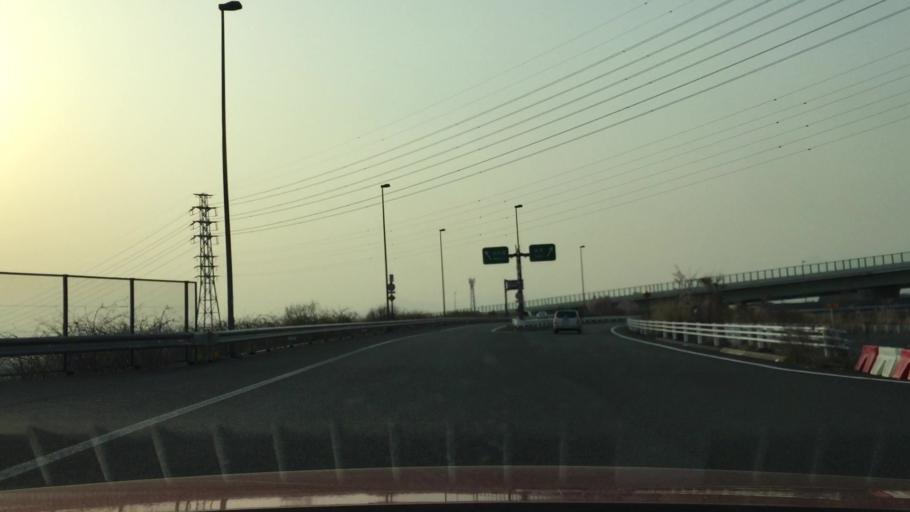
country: JP
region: Shizuoka
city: Fuji
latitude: 35.2008
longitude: 138.6625
